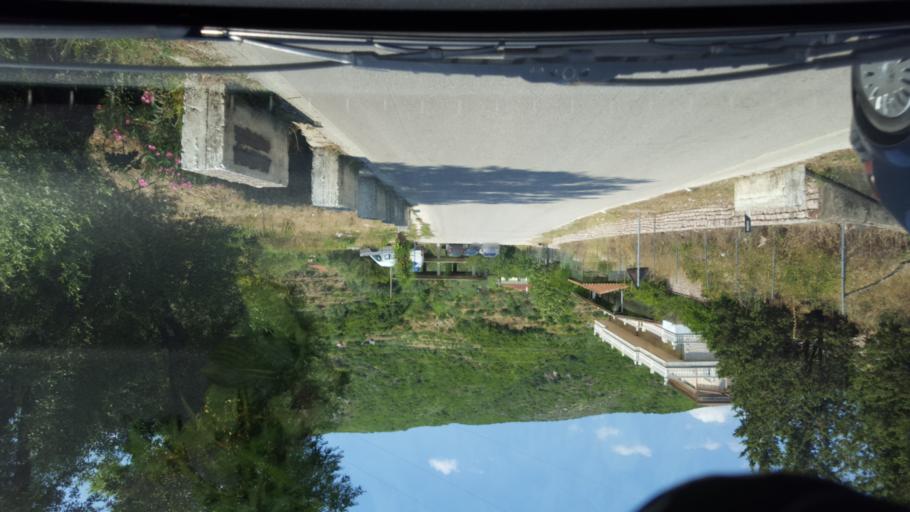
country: AL
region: Vlore
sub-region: Rrethi i Delvines
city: Mesopotam
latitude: 39.9169
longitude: 20.1352
